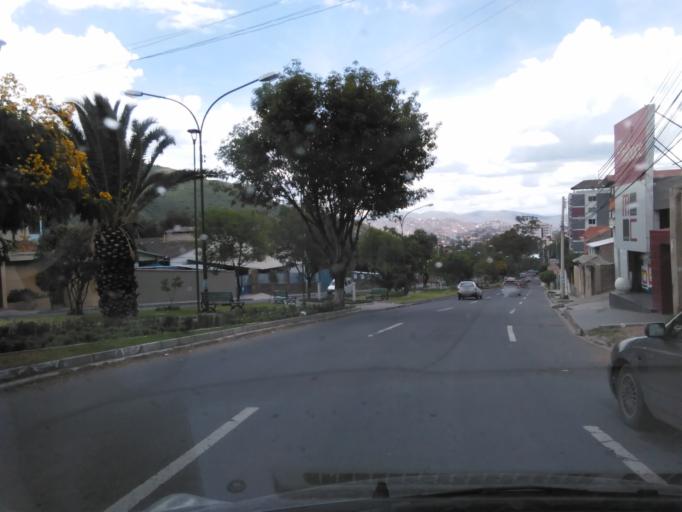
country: BO
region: Cochabamba
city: Cochabamba
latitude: -17.3706
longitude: -66.1424
